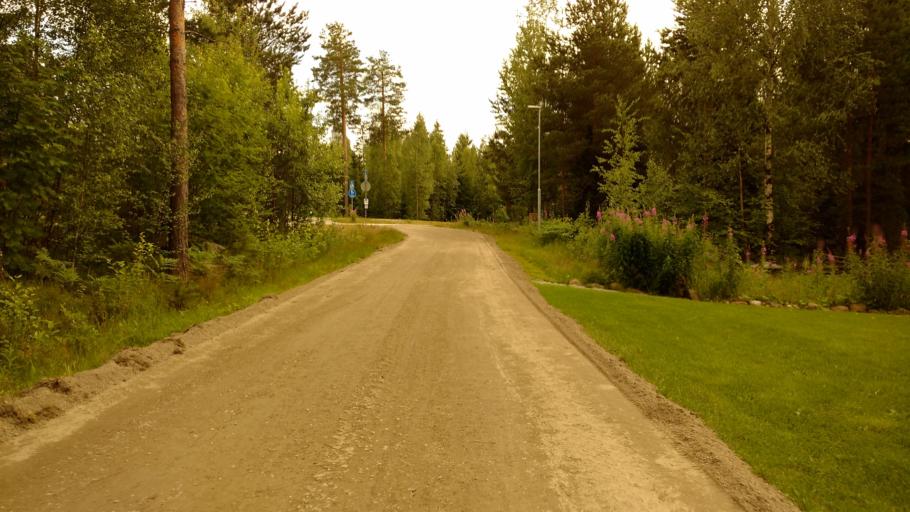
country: FI
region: Varsinais-Suomi
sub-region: Salo
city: Salo
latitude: 60.3980
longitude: 23.1866
